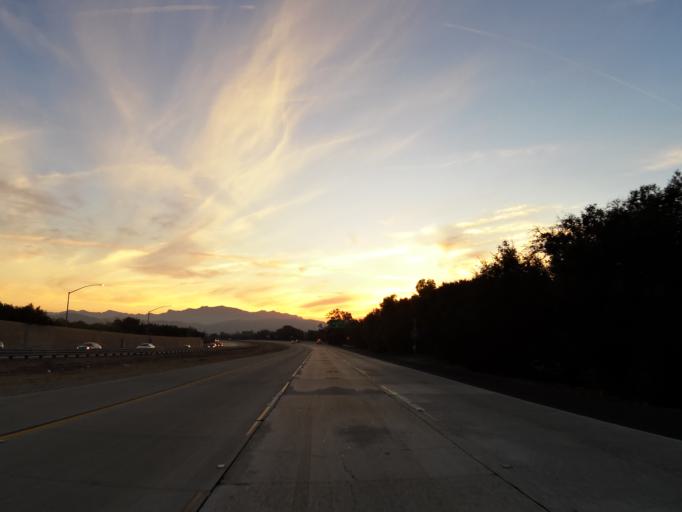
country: US
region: California
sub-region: Ventura County
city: Thousand Oaks
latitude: 34.2040
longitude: -118.8532
